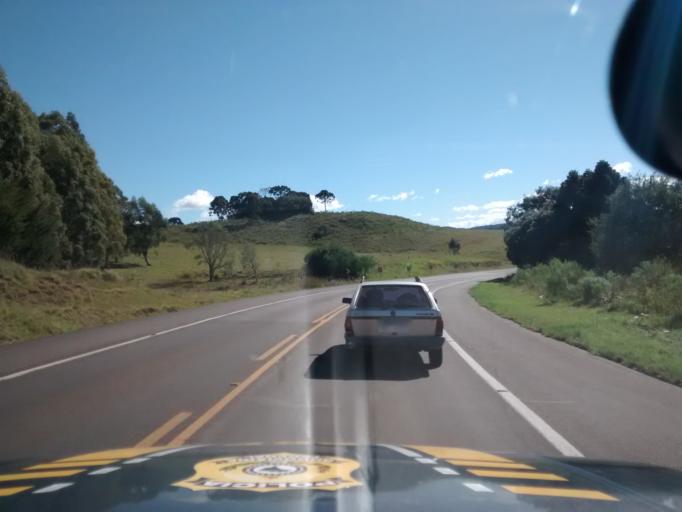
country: BR
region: Rio Grande do Sul
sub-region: Vacaria
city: Vacaria
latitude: -28.3536
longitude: -51.1409
